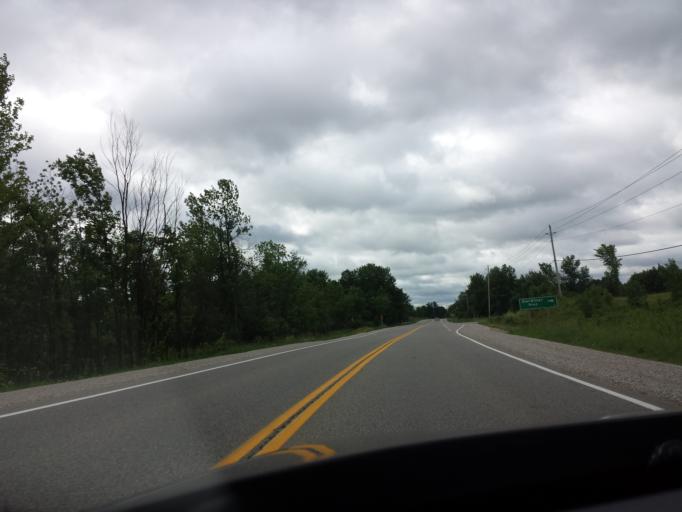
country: CA
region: Ontario
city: Perth
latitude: 45.0177
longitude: -76.2336
